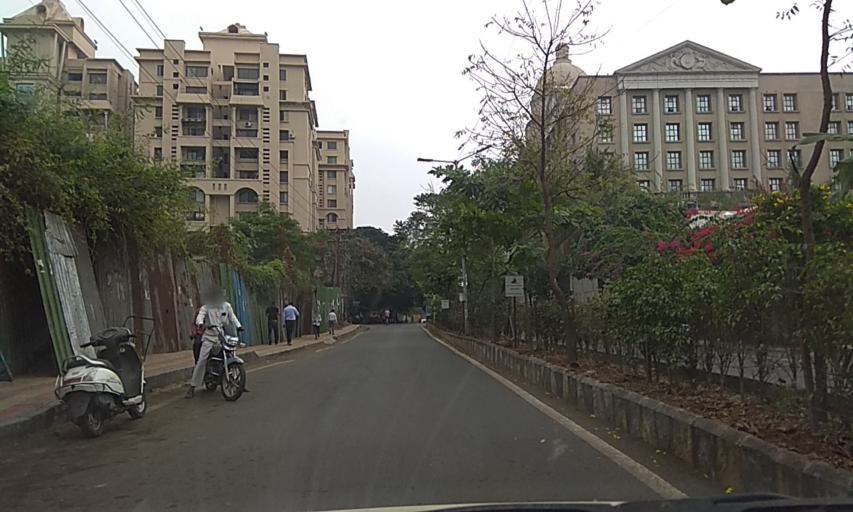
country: IN
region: Maharashtra
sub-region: Pune Division
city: Lohogaon
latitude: 18.5456
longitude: 73.9086
